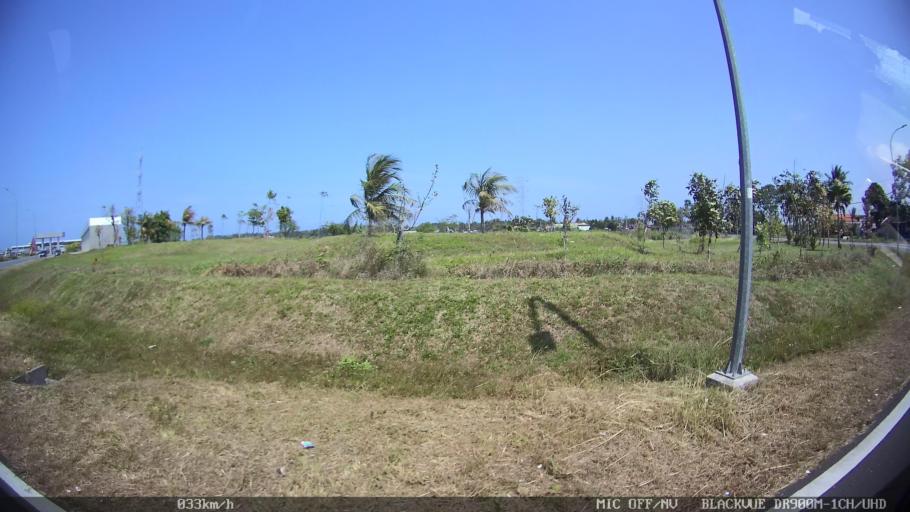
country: ID
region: Daerah Istimewa Yogyakarta
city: Srandakan
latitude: -7.8871
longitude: 110.0634
